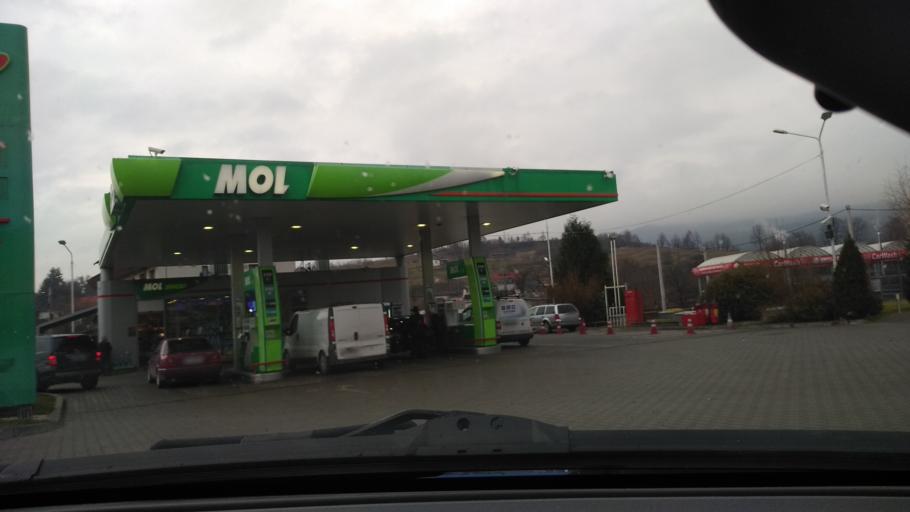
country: RO
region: Mures
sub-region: Oras Sovata
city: Sovata
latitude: 46.5819
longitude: 25.0557
